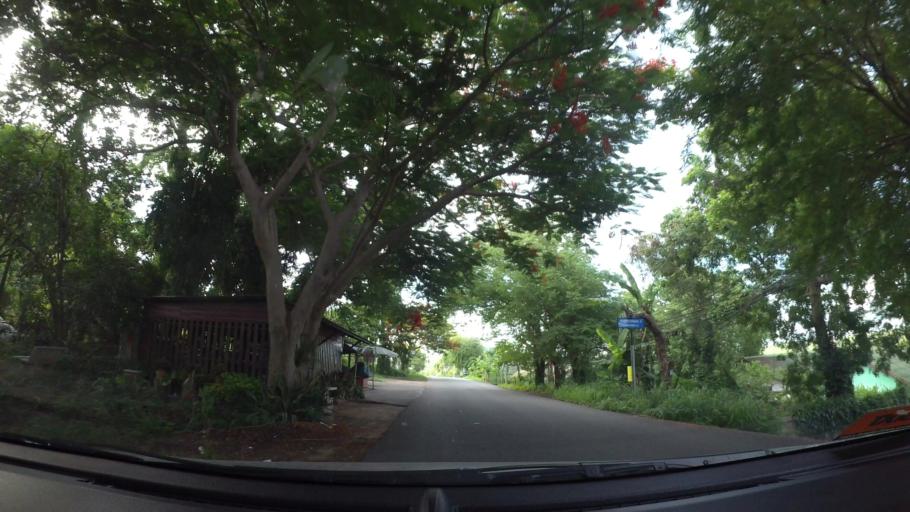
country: TH
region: Chon Buri
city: Sattahip
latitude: 12.6708
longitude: 100.9283
